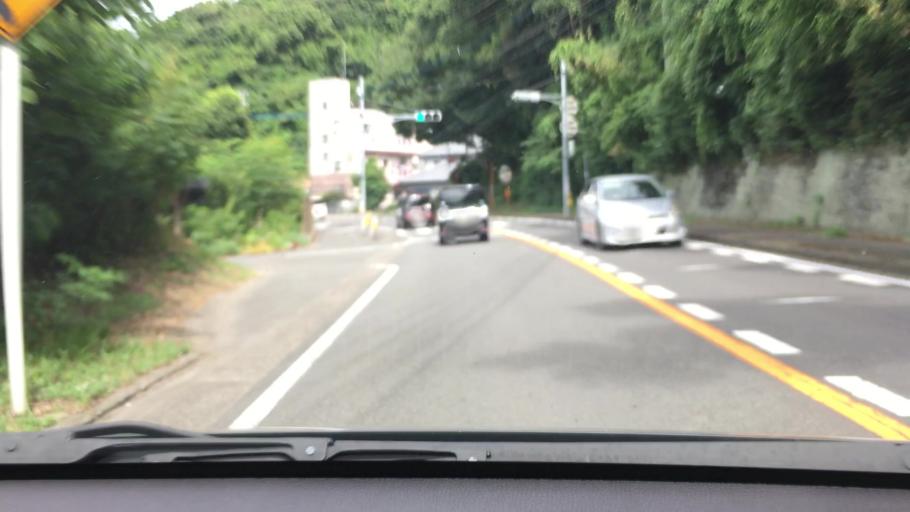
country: JP
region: Nagasaki
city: Togitsu
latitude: 32.8607
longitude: 129.7971
